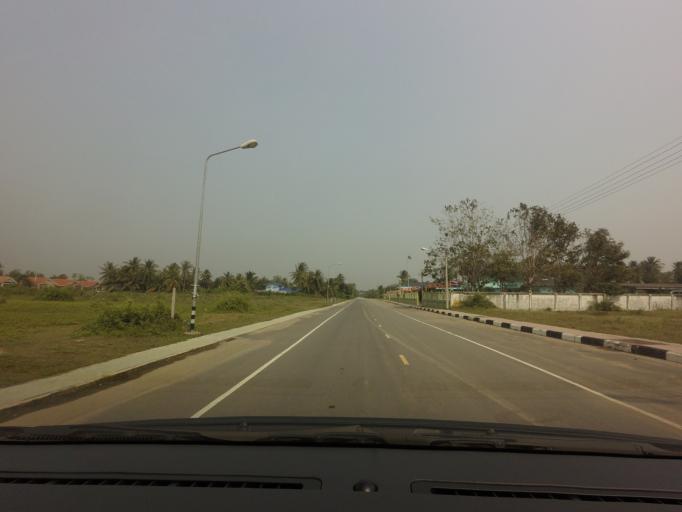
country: TH
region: Prachuap Khiri Khan
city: Kui Buri
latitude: 12.0705
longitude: 99.8662
